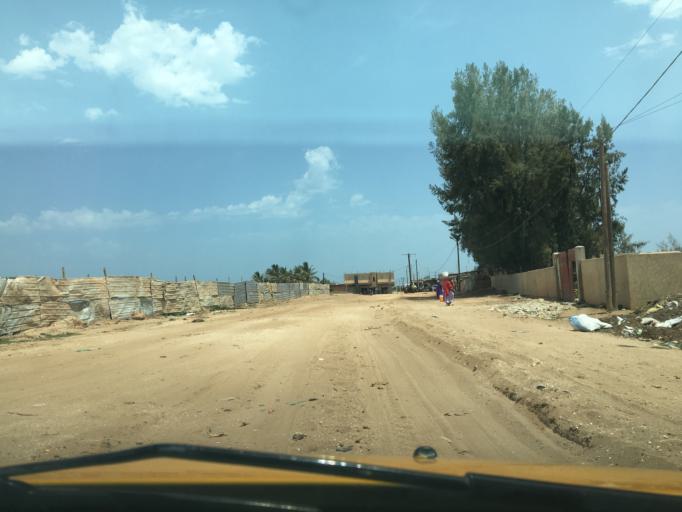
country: SN
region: Thies
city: Thies
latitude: 14.8057
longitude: -17.1870
